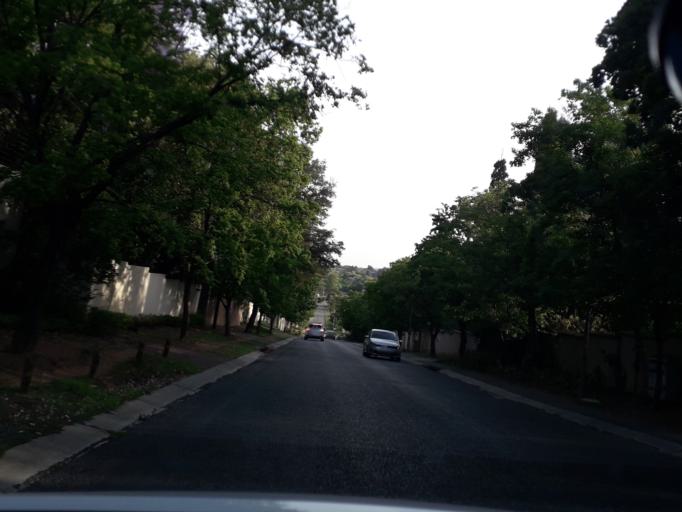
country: ZA
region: Gauteng
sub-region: City of Johannesburg Metropolitan Municipality
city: Johannesburg
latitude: -26.0787
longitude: 27.9900
